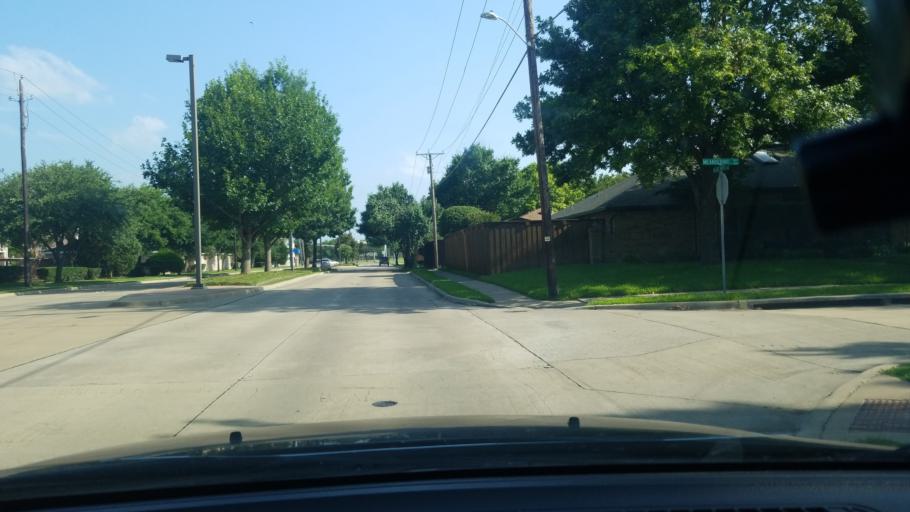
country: US
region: Texas
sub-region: Dallas County
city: Mesquite
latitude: 32.8154
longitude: -96.6074
